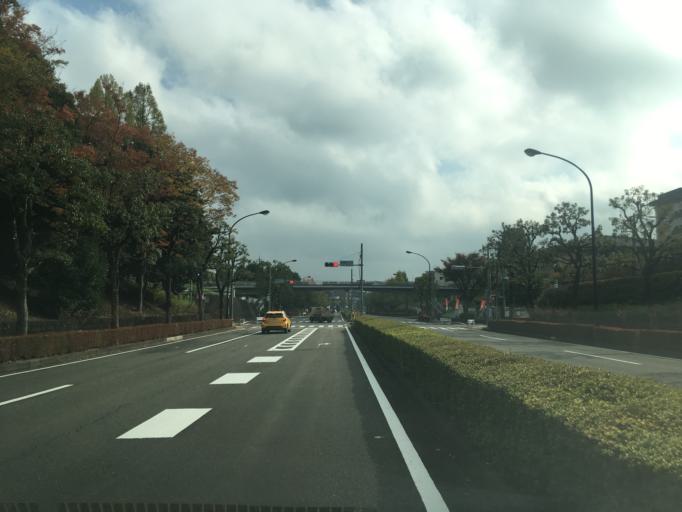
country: JP
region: Tokyo
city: Hino
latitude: 35.6129
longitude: 139.4233
